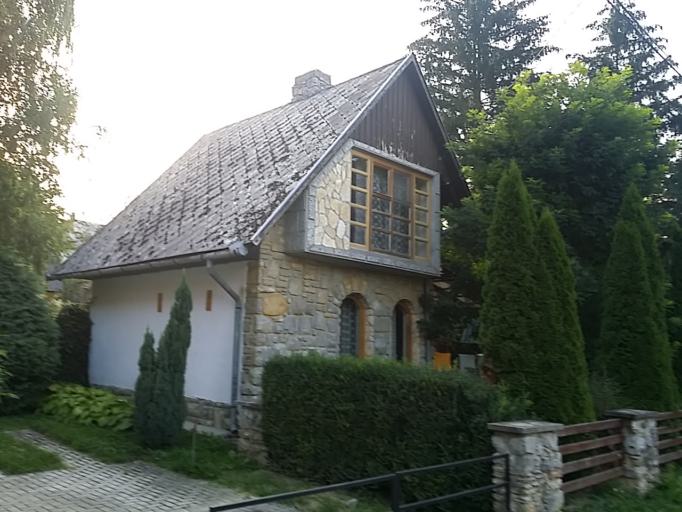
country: HU
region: Baranya
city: Pellerd
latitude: 46.1399
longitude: 18.1170
